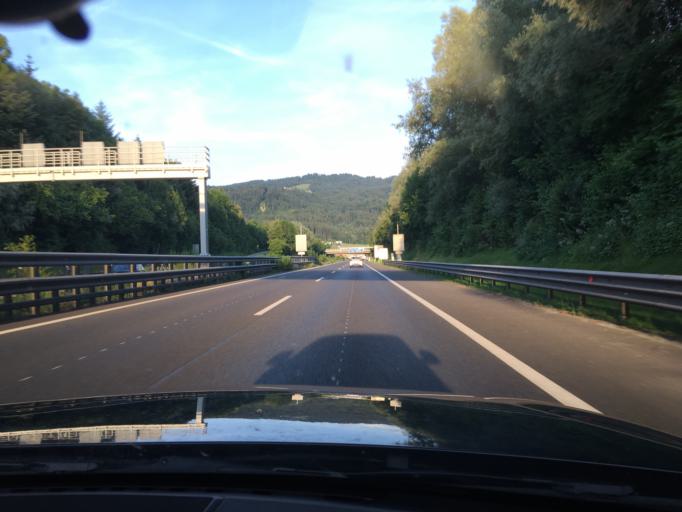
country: AT
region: Vorarlberg
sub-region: Politischer Bezirk Bregenz
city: Horbranz
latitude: 47.5431
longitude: 9.7444
